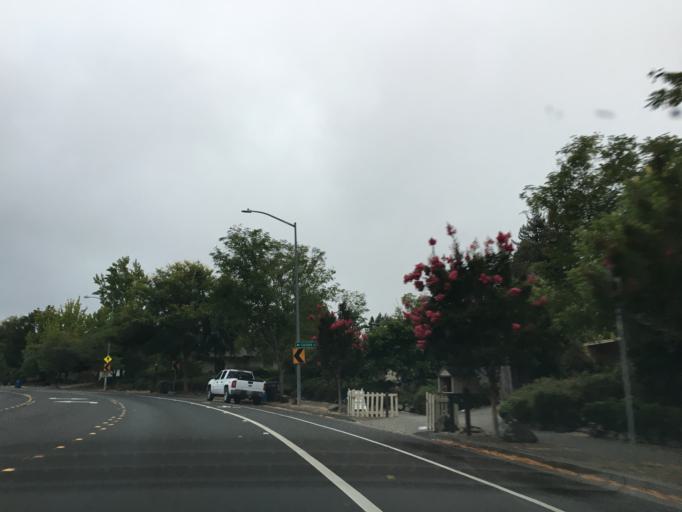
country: US
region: California
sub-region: Sonoma County
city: Santa Rosa
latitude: 38.4667
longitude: -122.6768
